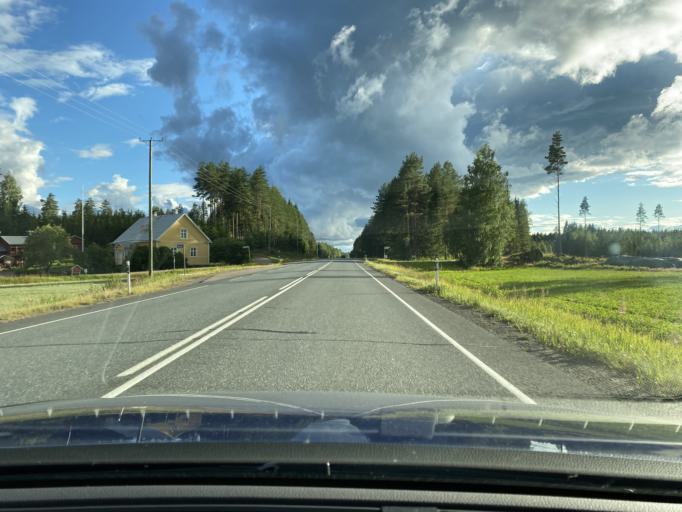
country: FI
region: Haeme
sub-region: Haemeenlinna
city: Renko
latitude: 60.8753
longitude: 24.2214
